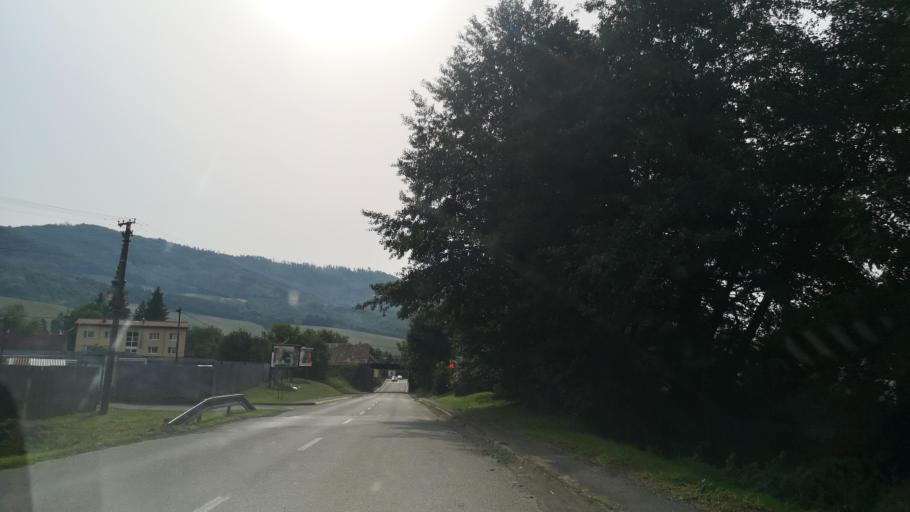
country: SK
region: Banskobystricky
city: Poltar
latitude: 48.5719
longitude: 19.8355
